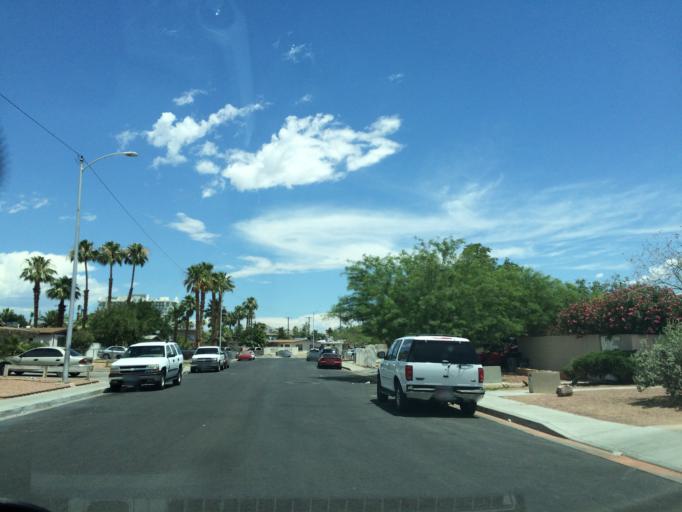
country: US
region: Nevada
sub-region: Clark County
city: Las Vegas
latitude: 36.1534
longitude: -115.1496
